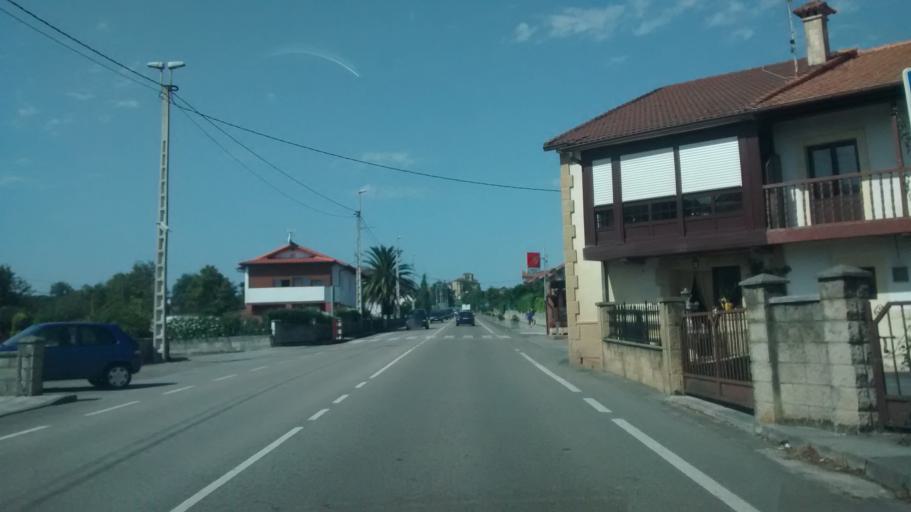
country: ES
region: Cantabria
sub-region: Provincia de Cantabria
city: Arnuero
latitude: 43.4598
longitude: -3.5459
